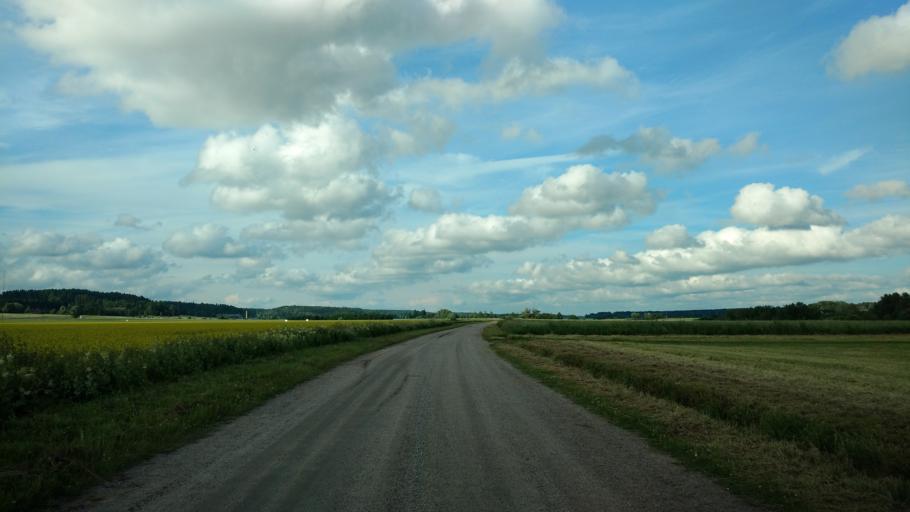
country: FI
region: Varsinais-Suomi
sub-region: Salo
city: Salo
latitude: 60.4017
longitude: 23.1549
